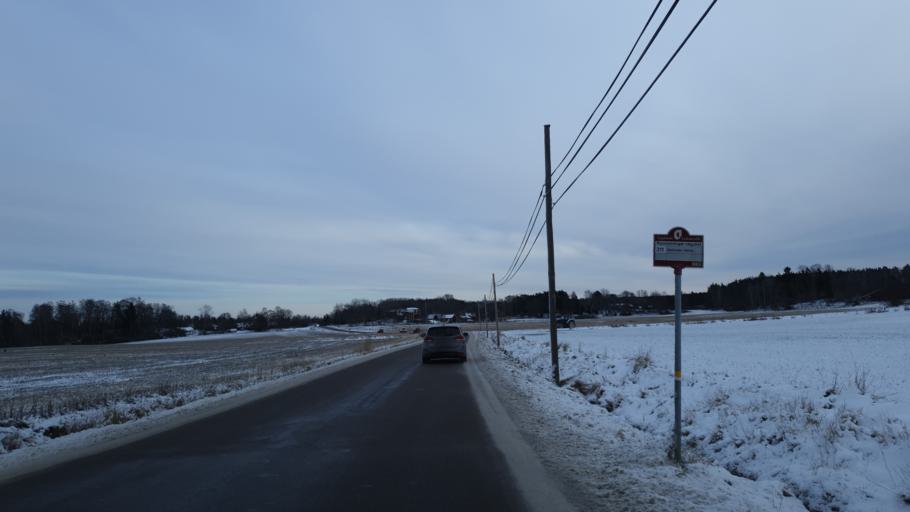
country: SE
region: Uppsala
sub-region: Habo Kommun
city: Balsta
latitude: 59.7079
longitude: 17.5796
